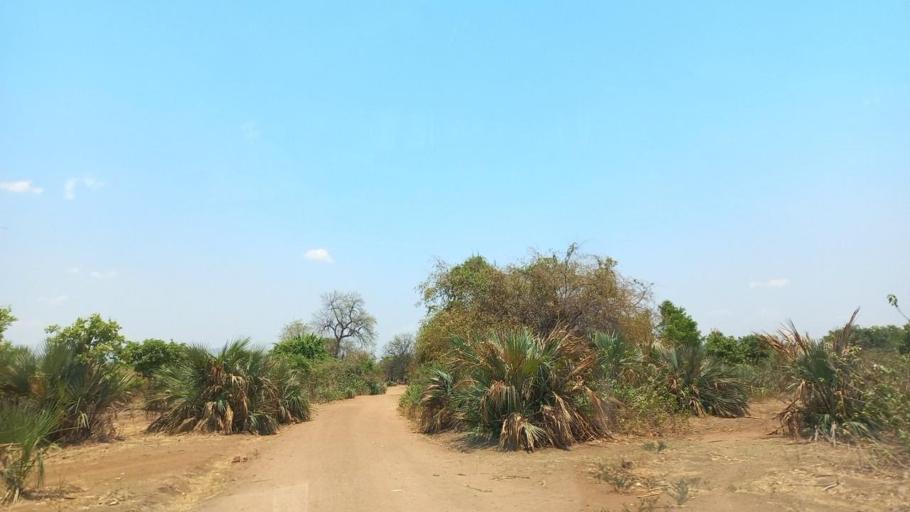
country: ZM
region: Lusaka
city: Luangwa
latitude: -15.1928
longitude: 30.1900
